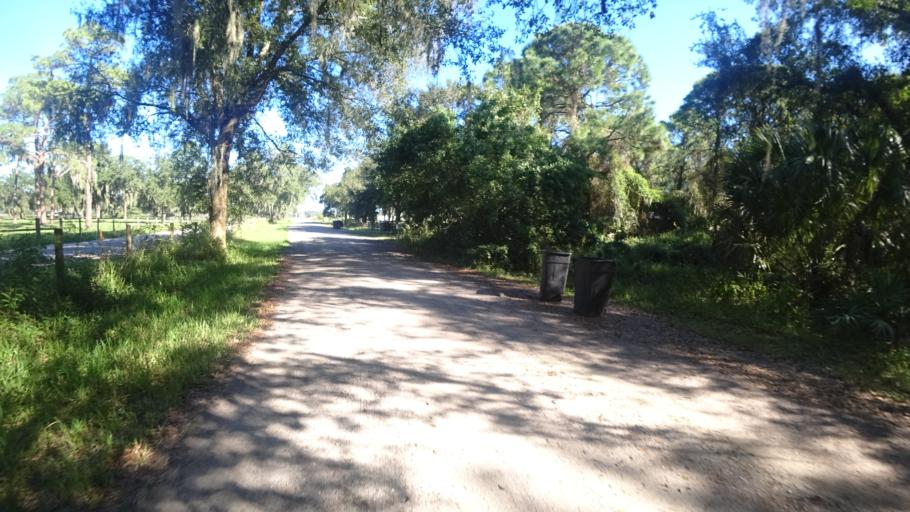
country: US
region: Florida
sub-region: Manatee County
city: Ellenton
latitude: 27.5749
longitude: -82.4418
